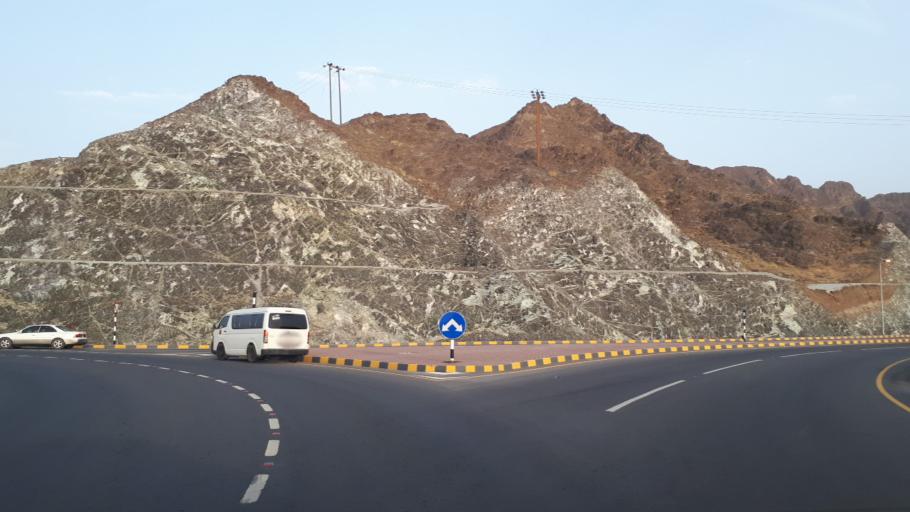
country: OM
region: Al Batinah
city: Rustaq
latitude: 23.4129
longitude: 57.3080
